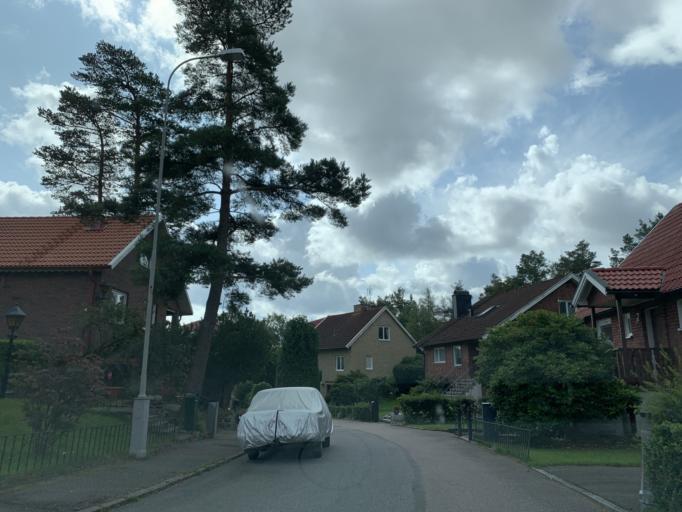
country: SE
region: Vaestra Goetaland
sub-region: Goteborg
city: Eriksbo
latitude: 57.7592
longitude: 12.0310
